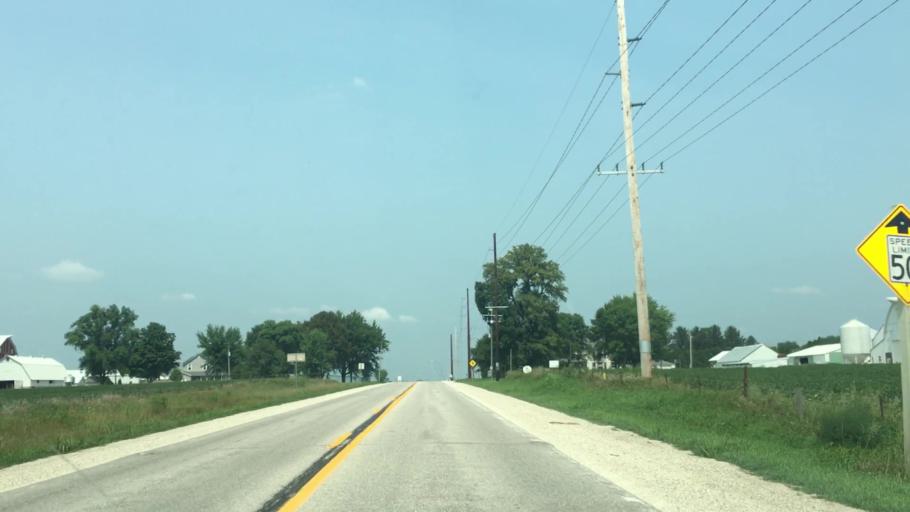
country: US
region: Iowa
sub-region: Buchanan County
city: Independence
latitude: 42.4407
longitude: -91.8900
